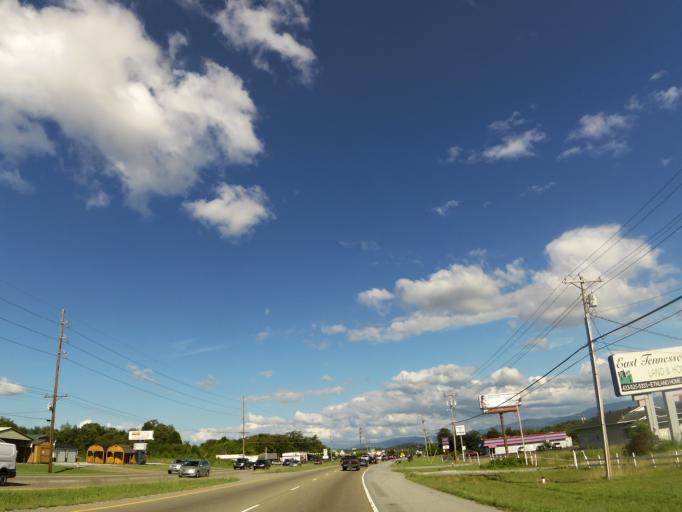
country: US
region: Tennessee
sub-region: Greene County
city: Greeneville
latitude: 36.1801
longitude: -82.8144
